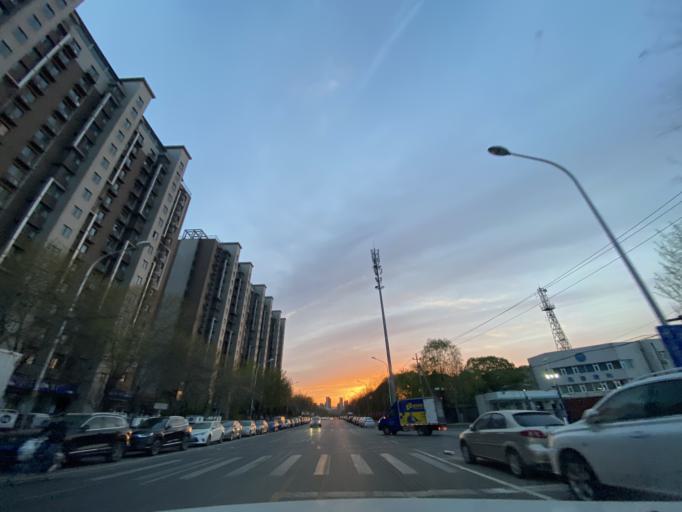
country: CN
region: Beijing
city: Qinghe
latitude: 40.0163
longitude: 116.3596
